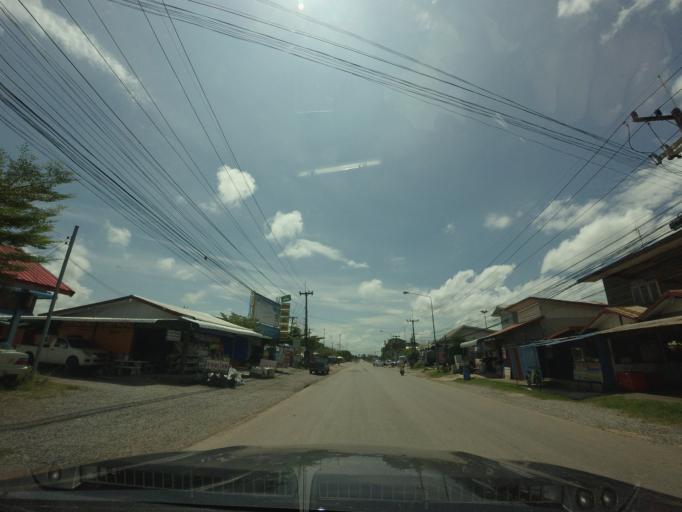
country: TH
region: Nong Khai
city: Pho Tak
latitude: 17.7776
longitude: 102.3950
